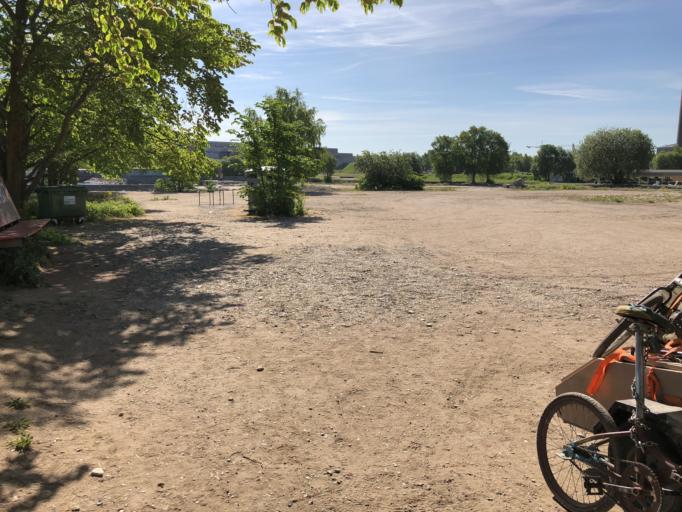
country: EE
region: Harju
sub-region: Tallinna linn
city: Tallinn
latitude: 59.4478
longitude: 24.7478
